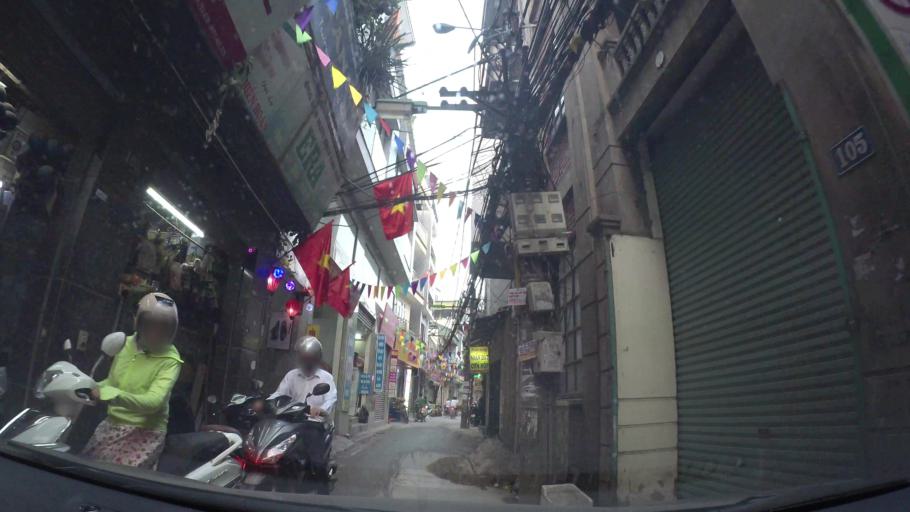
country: VN
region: Ha Noi
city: Thanh Xuan
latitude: 20.9805
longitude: 105.8019
